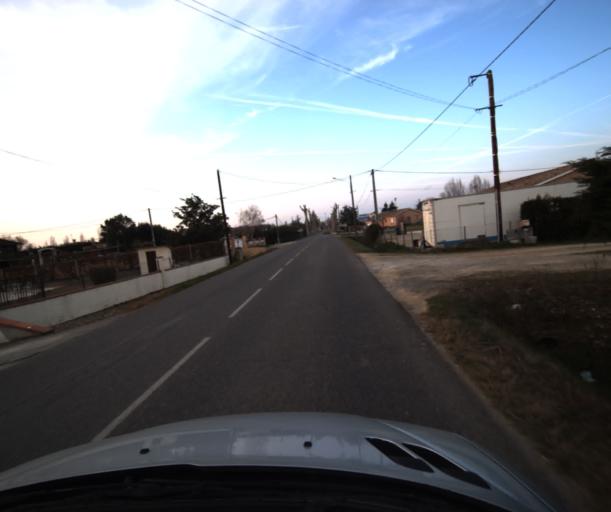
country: FR
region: Midi-Pyrenees
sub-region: Departement du Tarn-et-Garonne
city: Labastide-Saint-Pierre
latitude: 43.9105
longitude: 1.3692
